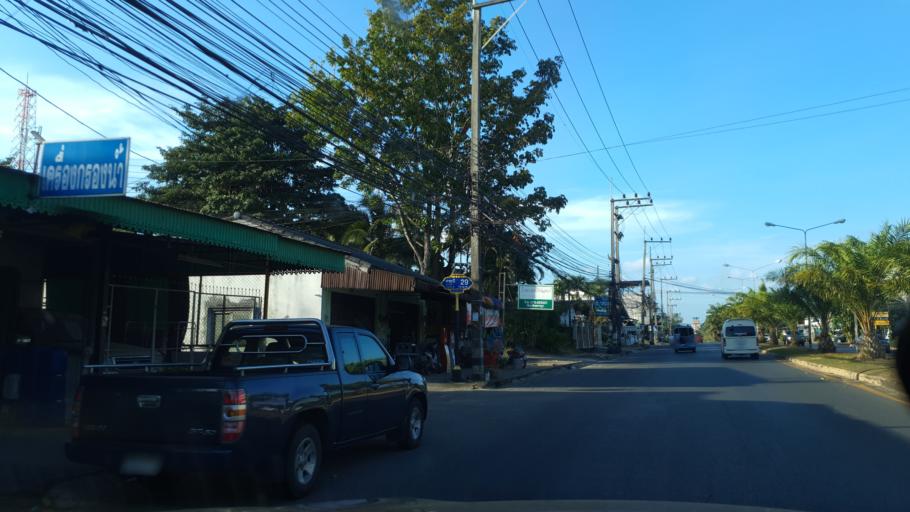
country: TH
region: Krabi
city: Krabi
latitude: 8.0694
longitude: 98.9068
